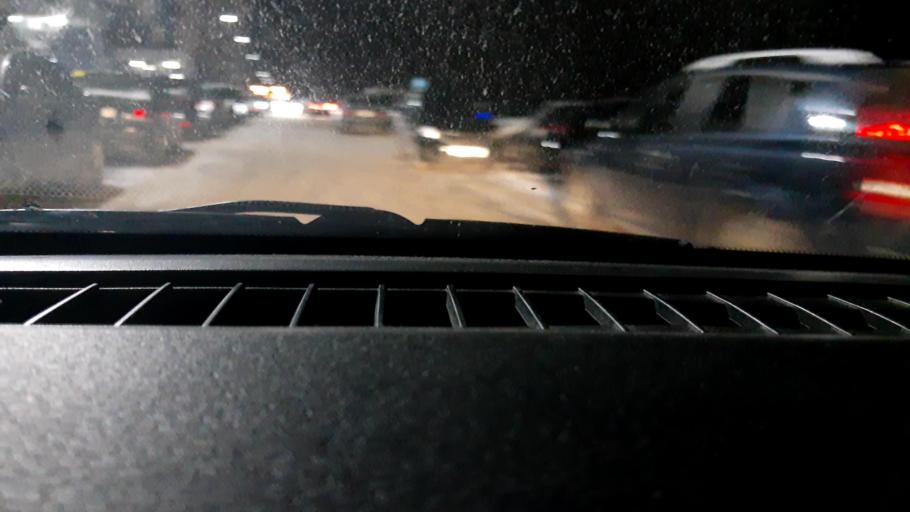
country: RU
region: Nizjnij Novgorod
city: Burevestnik
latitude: 56.2091
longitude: 43.8222
